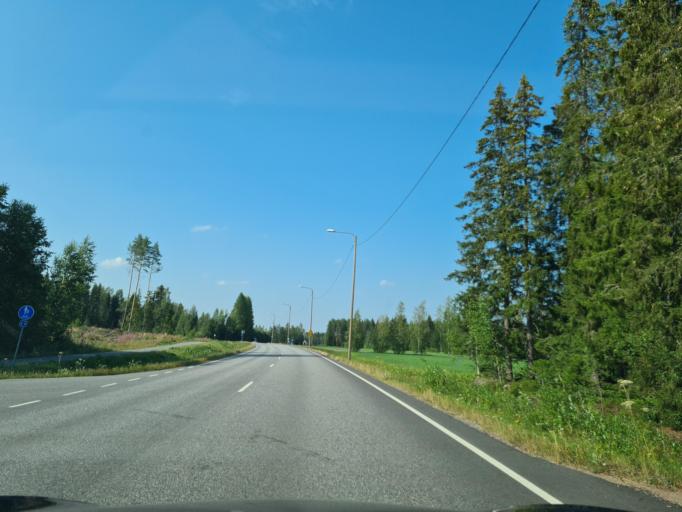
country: FI
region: Satakunta
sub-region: Pohjois-Satakunta
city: Karvia
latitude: 62.0864
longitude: 22.5270
